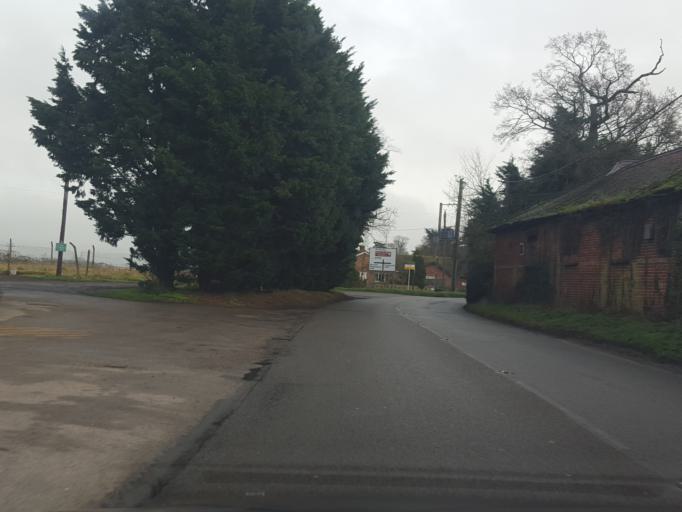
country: GB
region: England
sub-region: Suffolk
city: East Bergholt
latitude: 51.9284
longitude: 0.9837
